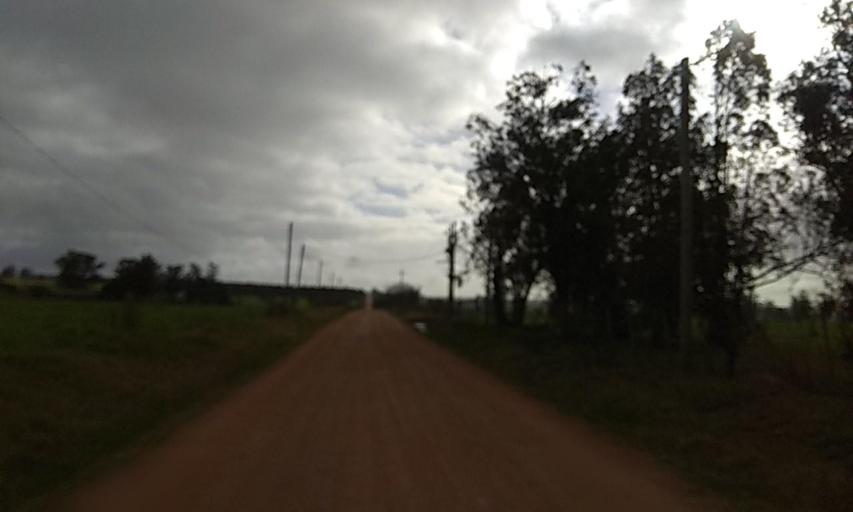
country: UY
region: Florida
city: Florida
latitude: -34.0735
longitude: -56.2332
